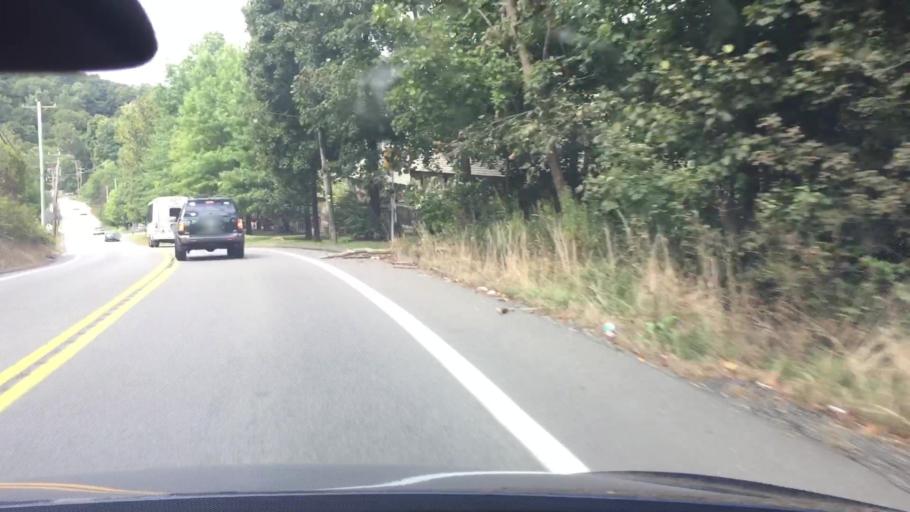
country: US
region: Pennsylvania
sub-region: Allegheny County
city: Cheswick
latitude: 40.5126
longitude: -79.8015
